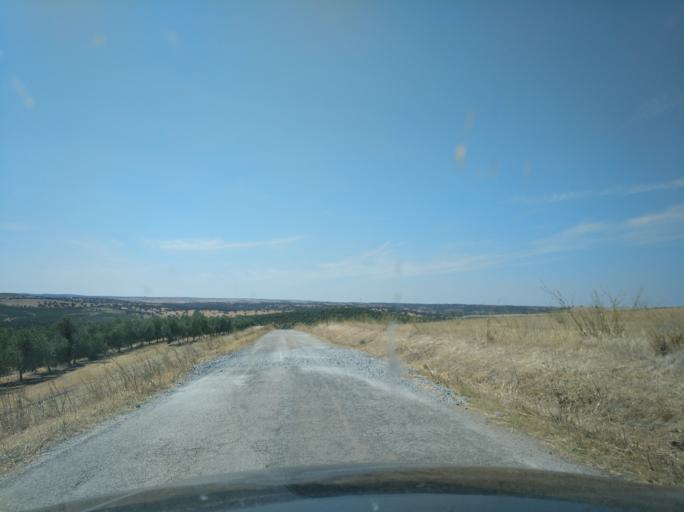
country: PT
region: Portalegre
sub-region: Campo Maior
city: Campo Maior
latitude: 38.9833
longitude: -7.0938
